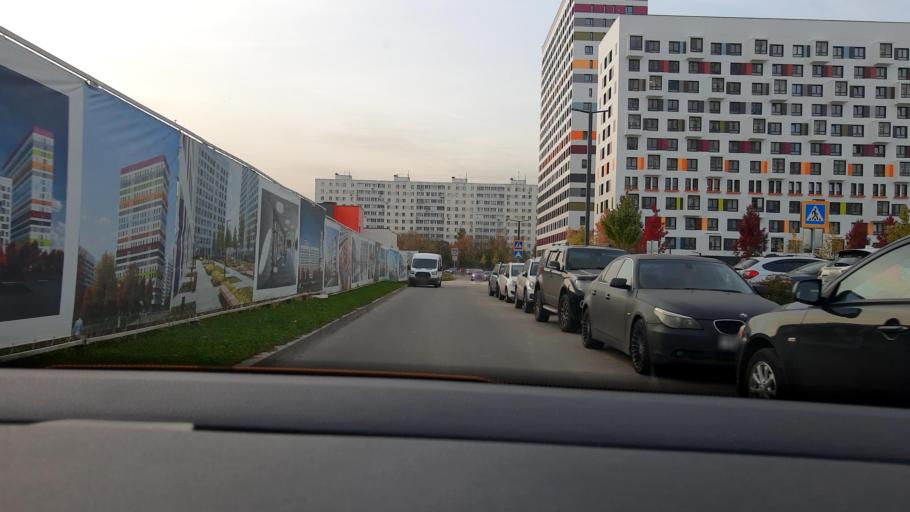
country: RU
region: Moscow
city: Sviblovo
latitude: 55.8511
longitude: 37.6223
